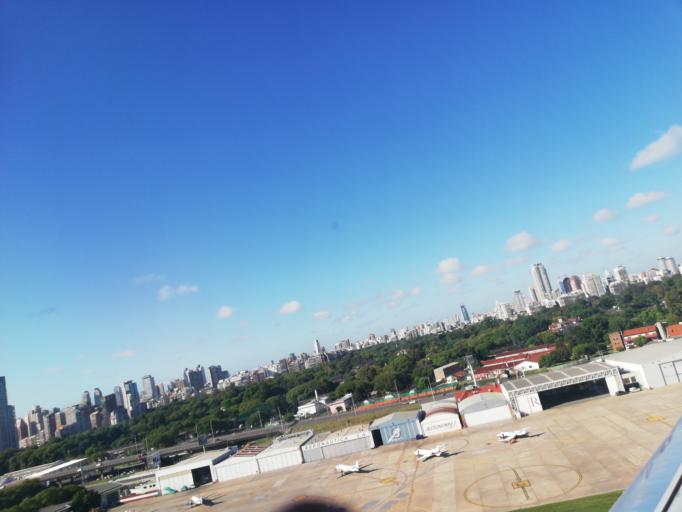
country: AR
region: Buenos Aires F.D.
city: Retiro
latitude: -34.5636
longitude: -58.4077
